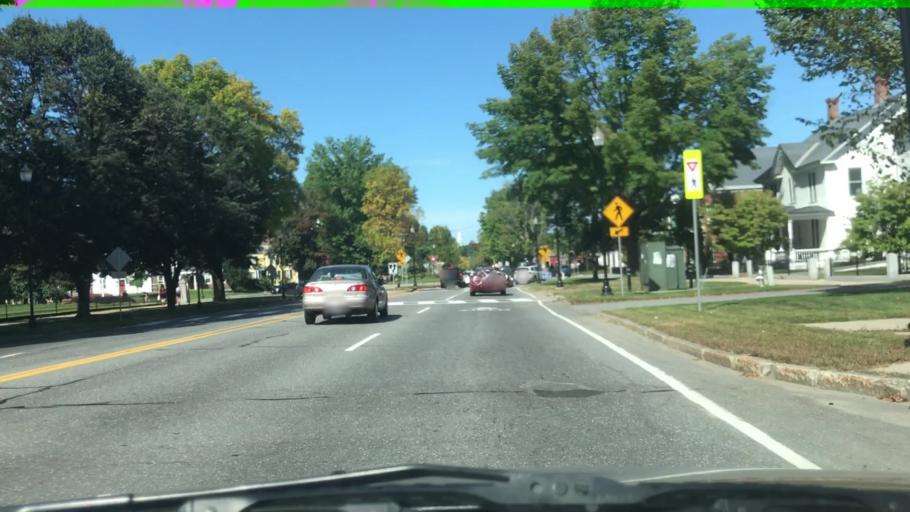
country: US
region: New Hampshire
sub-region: Cheshire County
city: Keene
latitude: 42.9275
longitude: -72.2774
